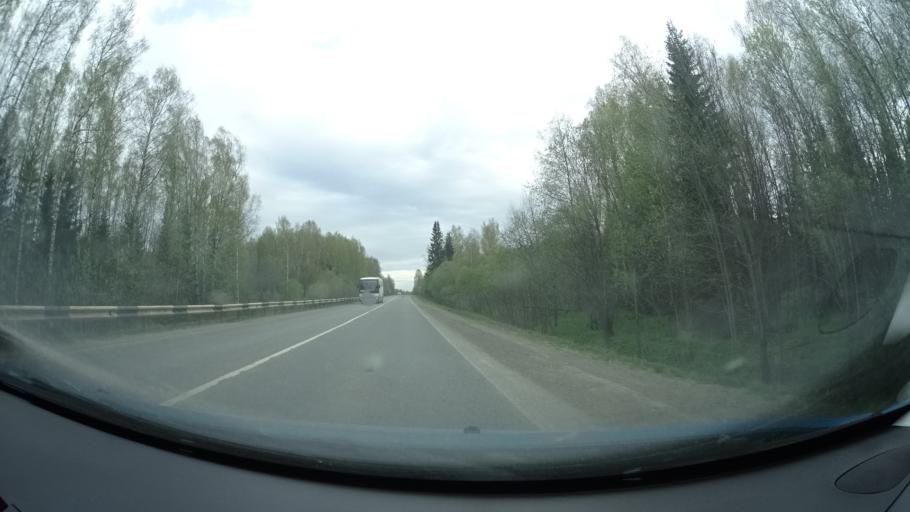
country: RU
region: Perm
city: Yugo-Kamskiy
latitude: 57.7414
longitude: 55.7118
